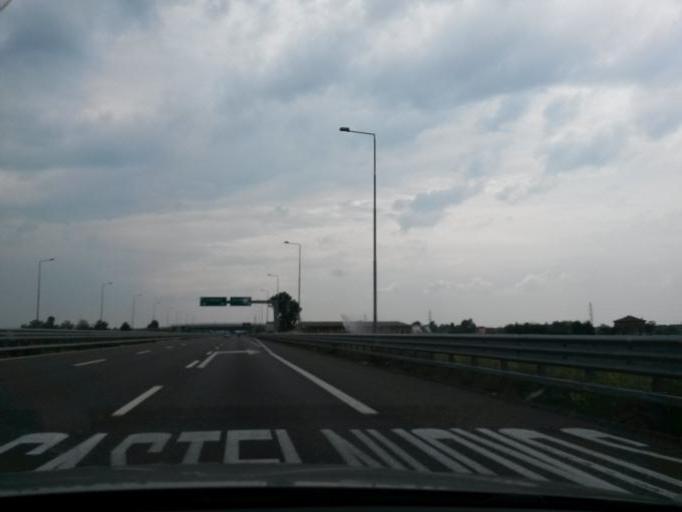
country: IT
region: Piedmont
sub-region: Provincia di Alessandria
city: Castelnuovo Scrivia
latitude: 44.9838
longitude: 8.9018
